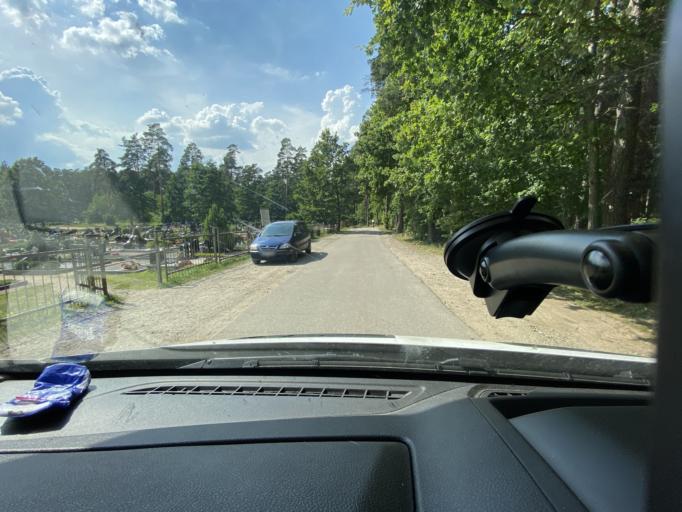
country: LT
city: Ramuciai
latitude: 54.9755
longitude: 24.0408
